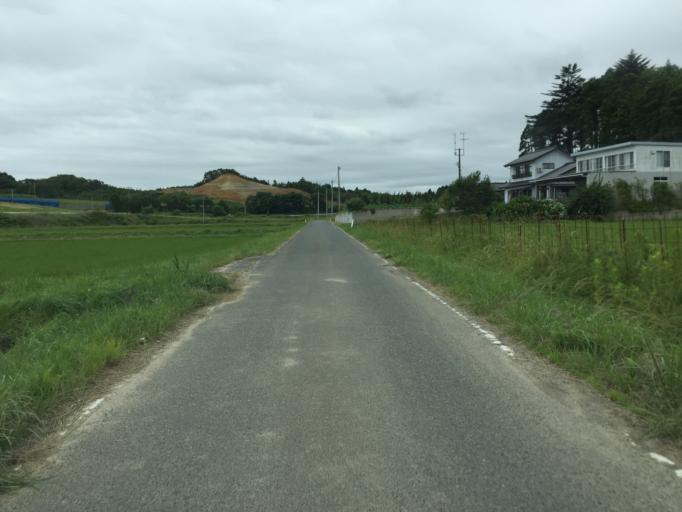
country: JP
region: Fukushima
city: Namie
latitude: 37.7491
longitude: 140.9932
